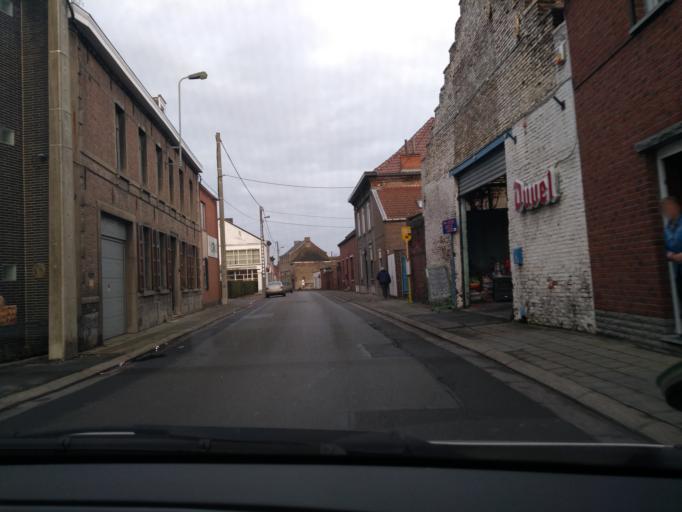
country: BE
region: Wallonia
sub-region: Province du Hainaut
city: Colfontaine
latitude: 50.4137
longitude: 3.8642
